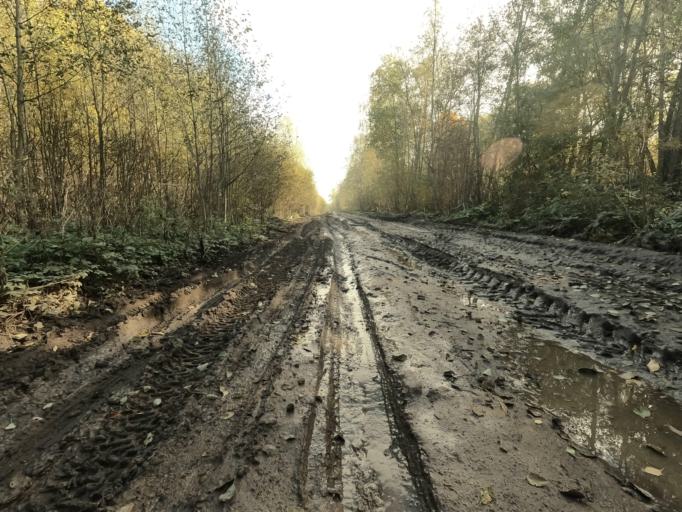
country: RU
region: Novgorod
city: Batetskiy
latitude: 58.8800
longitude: 30.7315
